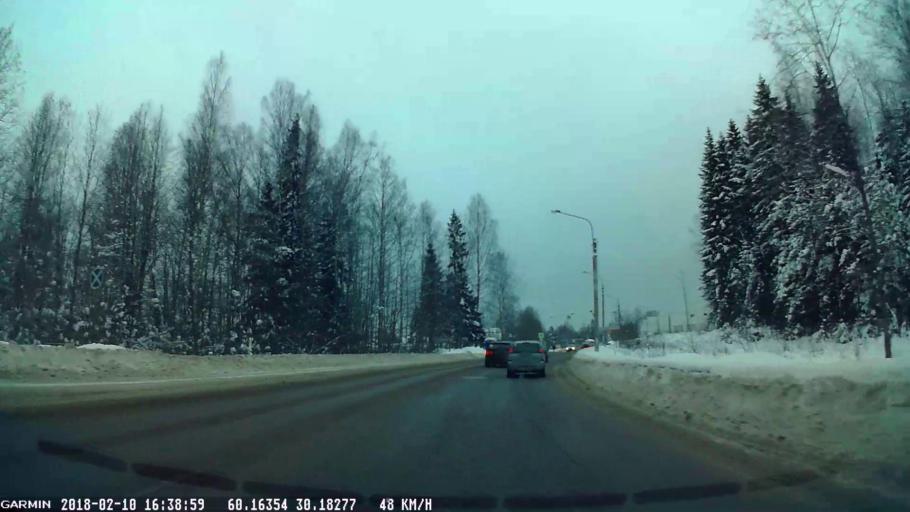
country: RU
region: Leningrad
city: Sertolovo
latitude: 60.1558
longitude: 30.1895
